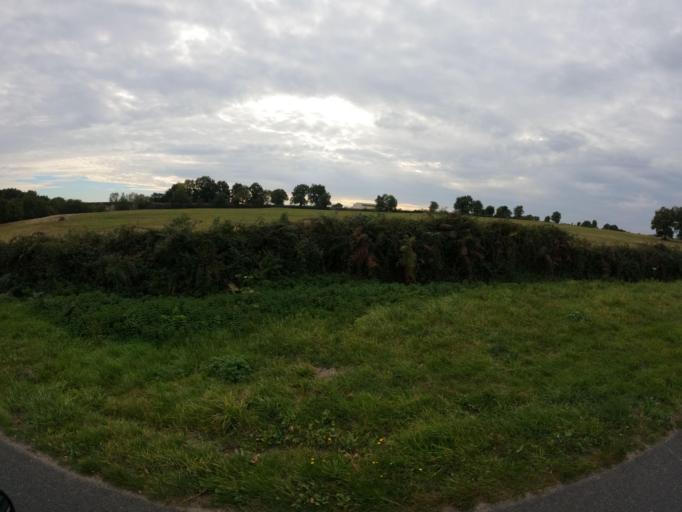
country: FR
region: Pays de la Loire
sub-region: Departement de Maine-et-Loire
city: Torfou
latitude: 47.0403
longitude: -1.1250
